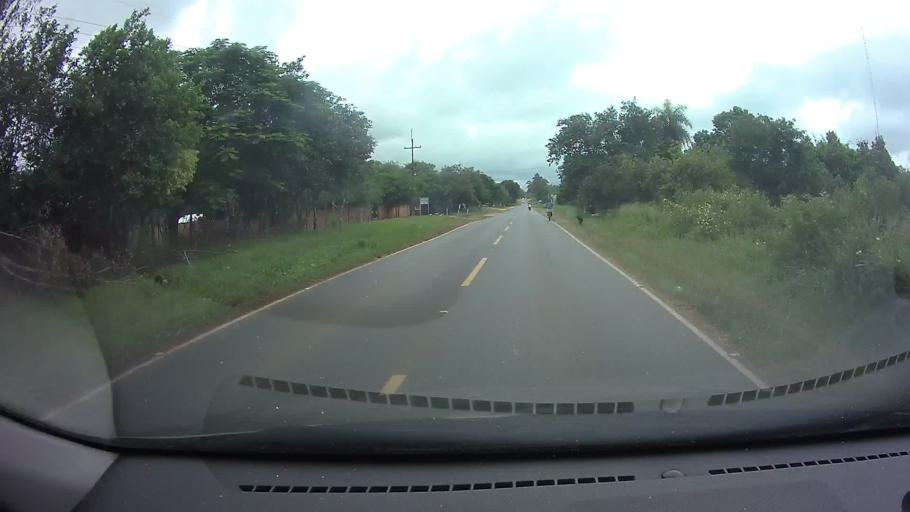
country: PY
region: Central
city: Guarambare
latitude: -25.5010
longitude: -57.4811
